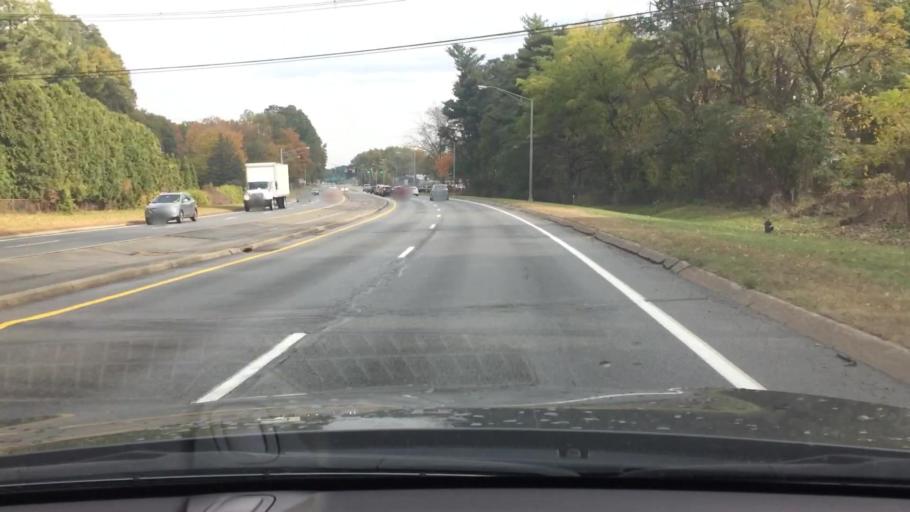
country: US
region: New York
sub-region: Saratoga County
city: Saratoga Springs
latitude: 43.0920
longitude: -73.7652
